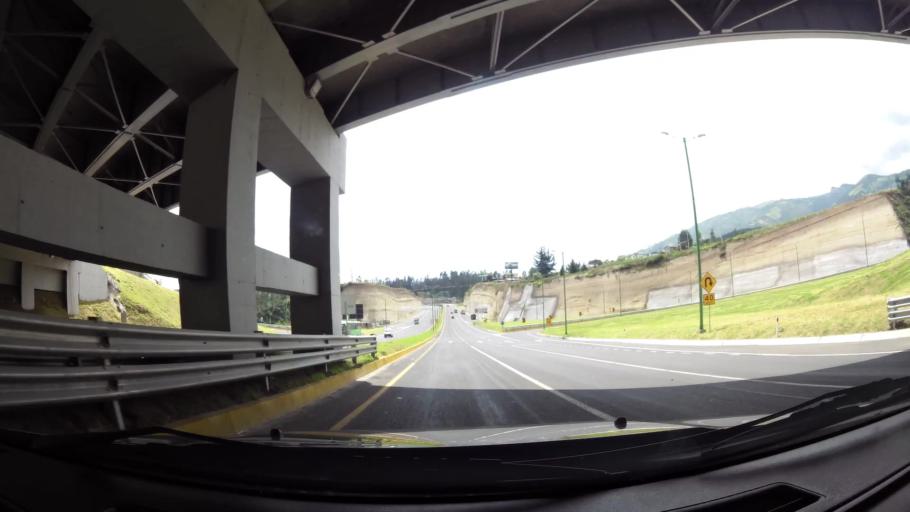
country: EC
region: Pichincha
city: Sangolqui
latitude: -0.2133
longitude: -78.3337
